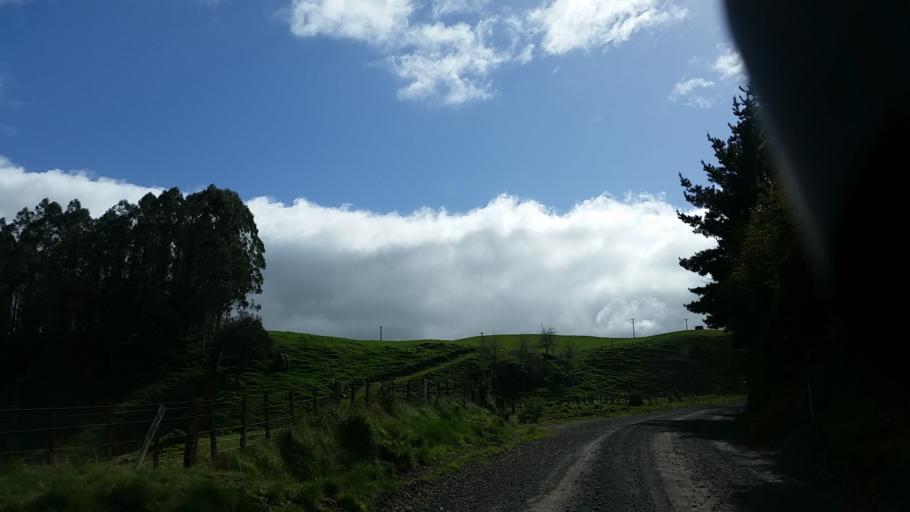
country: NZ
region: Bay of Plenty
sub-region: Rotorua District
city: Rotorua
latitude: -38.3740
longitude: 176.1209
